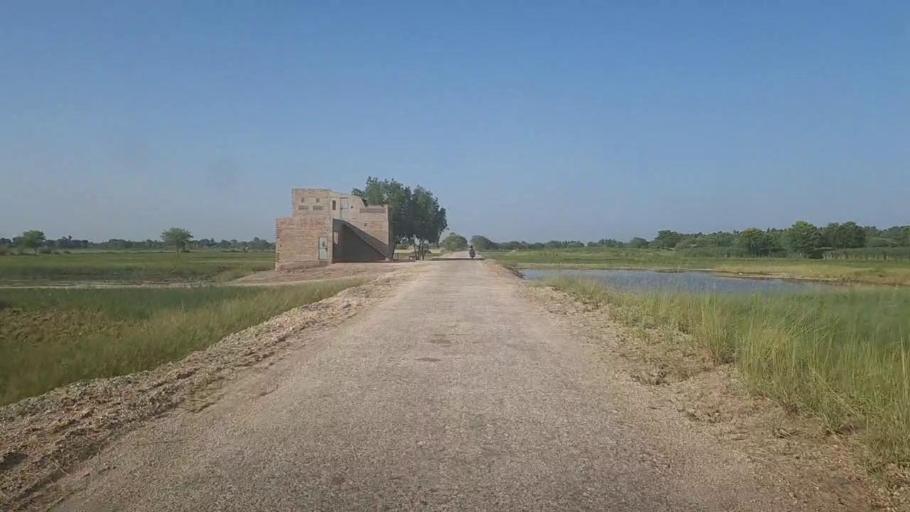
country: PK
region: Sindh
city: Khairpur
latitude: 28.1016
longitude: 69.6304
